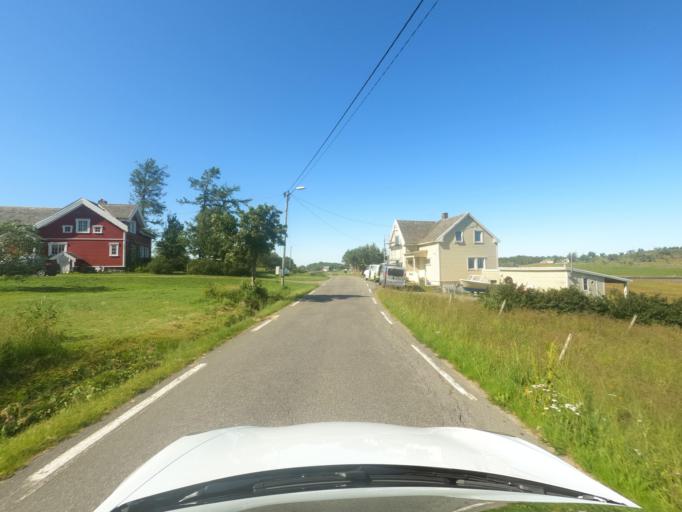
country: NO
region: Nordland
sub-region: Hadsel
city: Melbu
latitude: 68.4343
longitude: 14.7496
